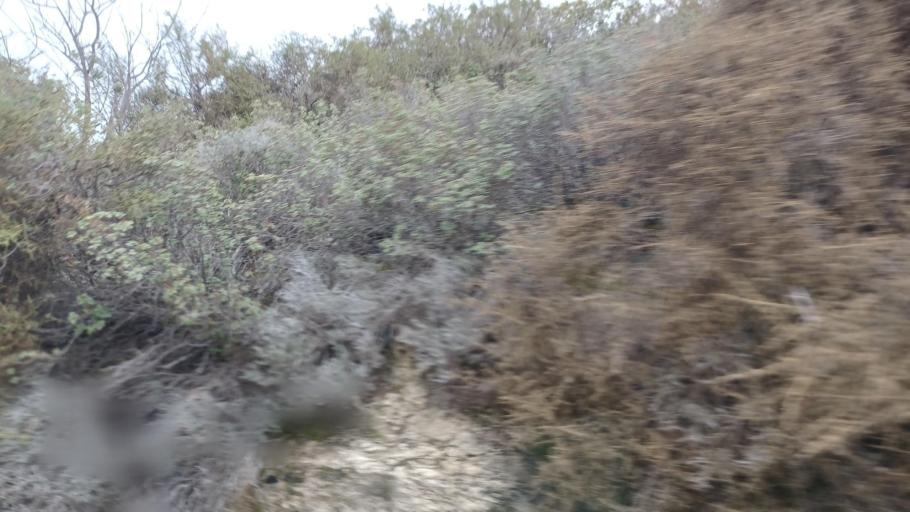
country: CY
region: Limassol
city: Pachna
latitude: 34.7519
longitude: 32.7349
